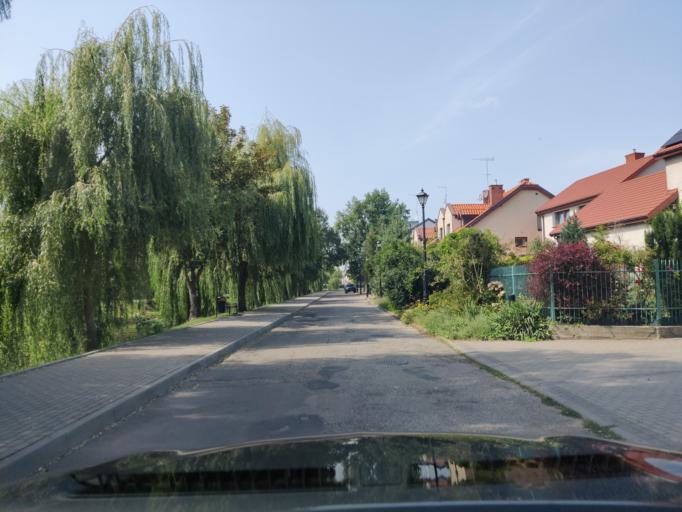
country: PL
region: Masovian Voivodeship
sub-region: Powiat pultuski
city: Pultusk
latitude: 52.7032
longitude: 21.0915
